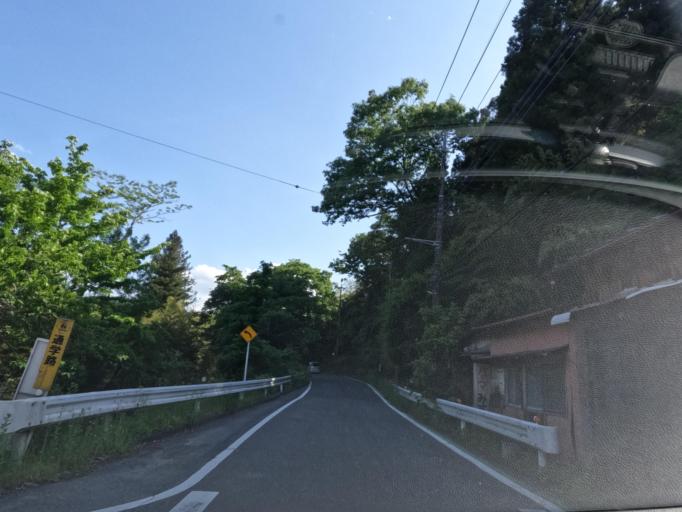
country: JP
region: Saitama
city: Chichibu
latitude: 36.0452
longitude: 139.1308
